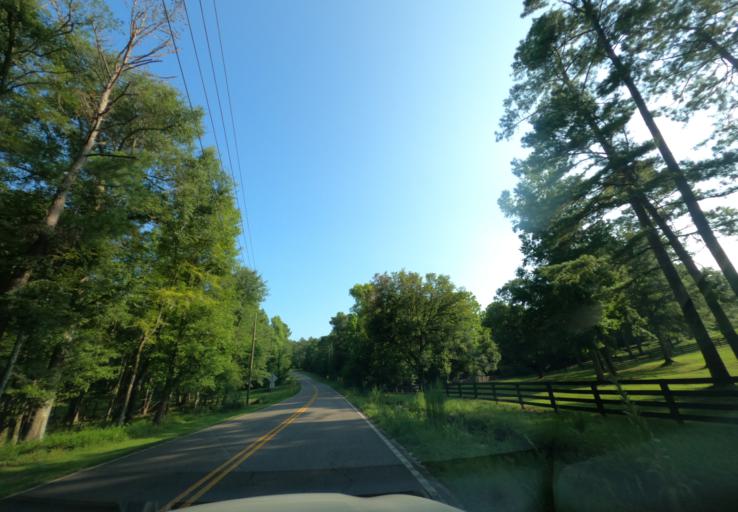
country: US
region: South Carolina
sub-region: Edgefield County
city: Murphys Estates
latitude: 33.6731
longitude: -81.9787
